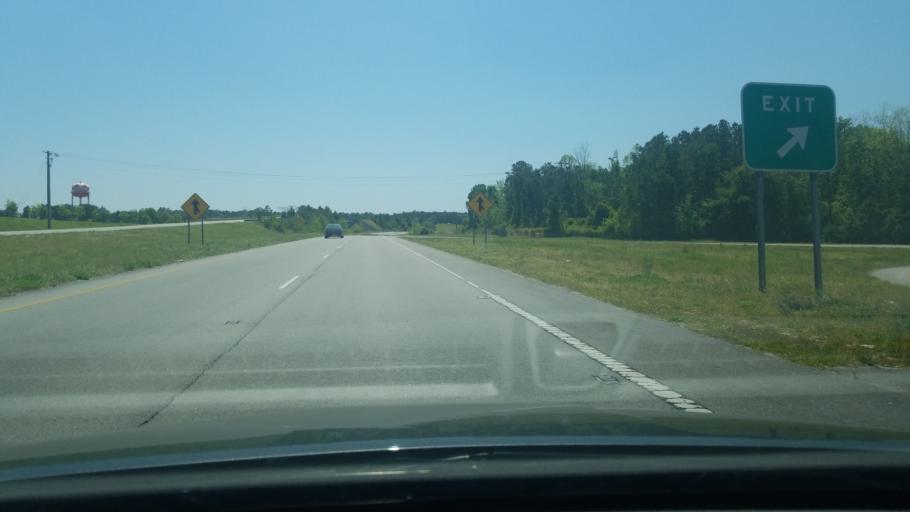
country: US
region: North Carolina
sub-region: Onslow County
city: Jacksonville
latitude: 34.7445
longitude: -77.4577
